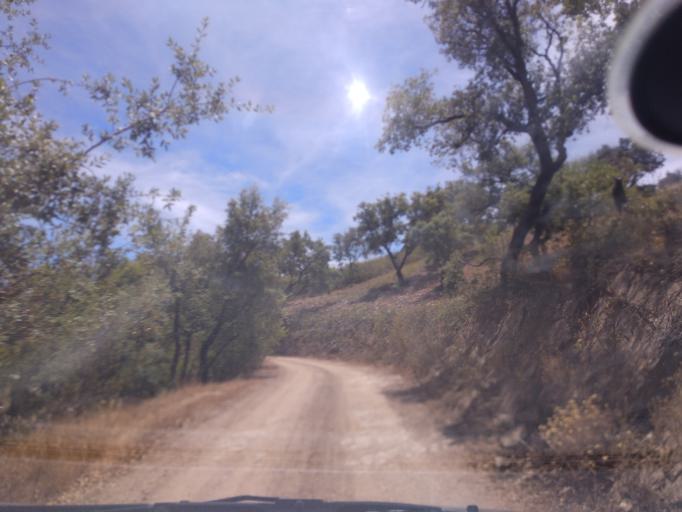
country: PT
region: Faro
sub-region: Sao Bras de Alportel
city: Sao Bras de Alportel
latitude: 37.2057
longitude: -7.8118
